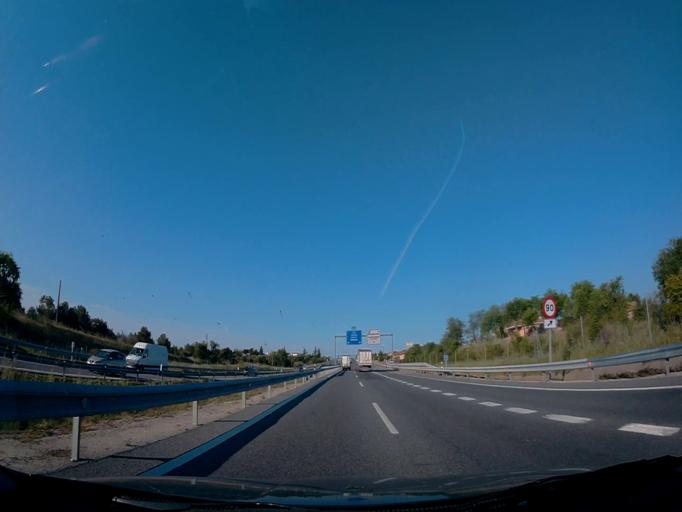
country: ES
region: Madrid
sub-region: Provincia de Madrid
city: Navalcarnero
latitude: 40.2551
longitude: -4.0499
